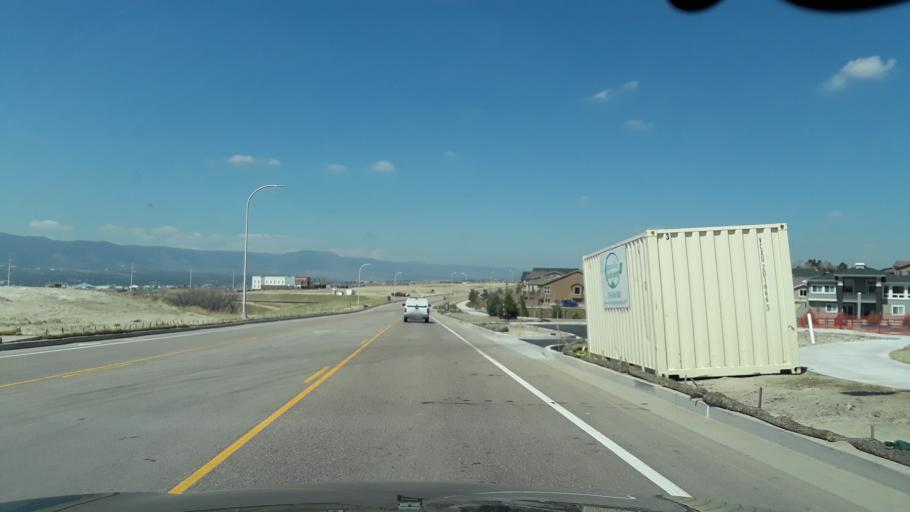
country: US
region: Colorado
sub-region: El Paso County
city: Black Forest
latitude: 38.9794
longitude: -104.7539
